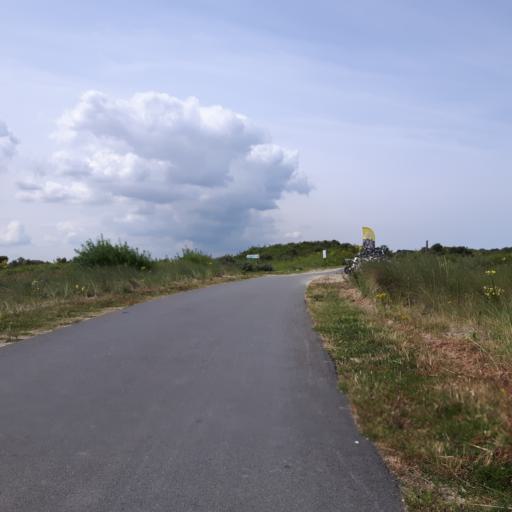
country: NL
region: Zeeland
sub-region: Gemeente Sluis
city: Sluis
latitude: 51.3891
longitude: 3.4222
